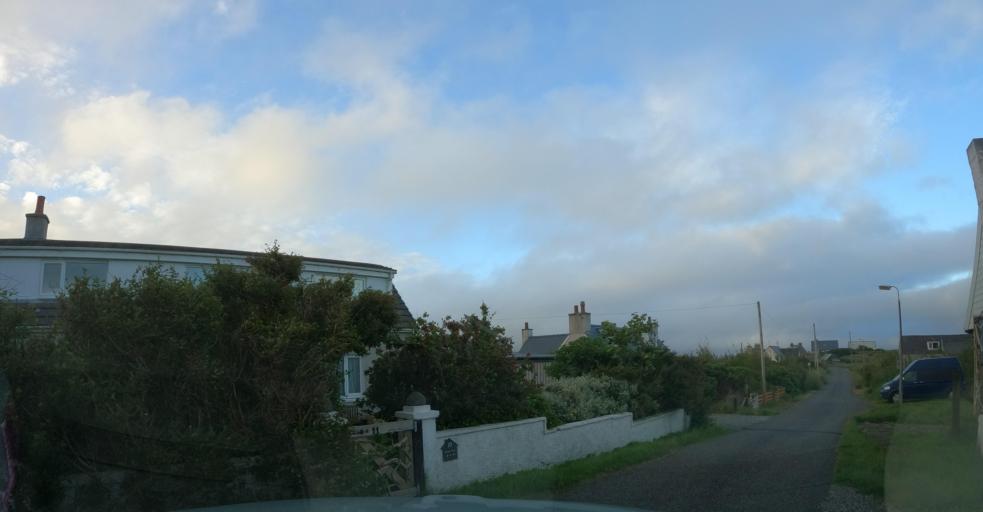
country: GB
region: Scotland
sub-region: Eilean Siar
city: Stornoway
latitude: 58.1944
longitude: -6.2173
